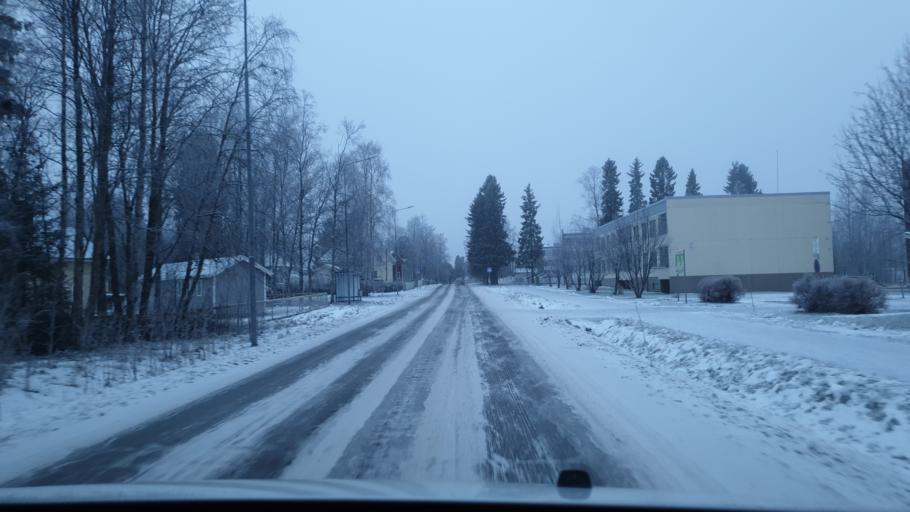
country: FI
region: Lapland
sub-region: Kemi-Tornio
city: Kemi
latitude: 65.7326
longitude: 24.6046
